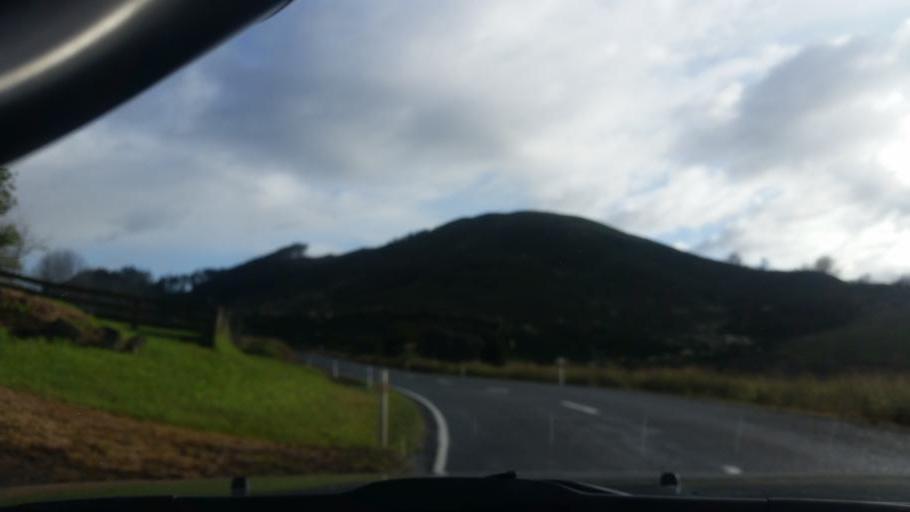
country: NZ
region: Northland
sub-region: Kaipara District
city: Dargaville
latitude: -35.7425
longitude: 173.8766
